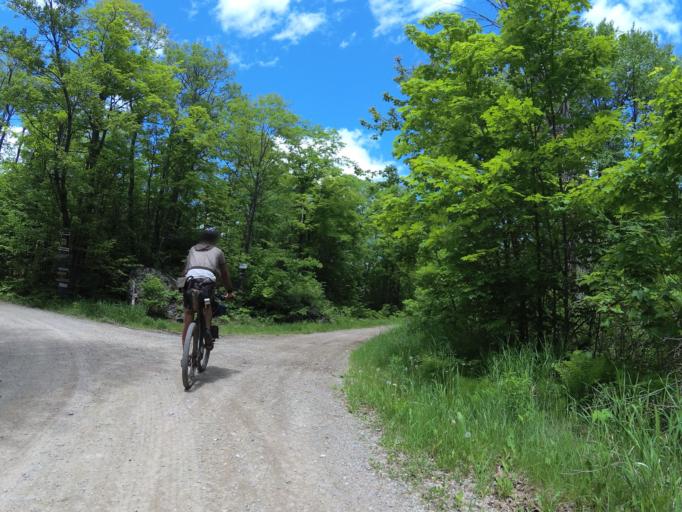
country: CA
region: Ontario
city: Renfrew
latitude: 45.0006
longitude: -76.9098
